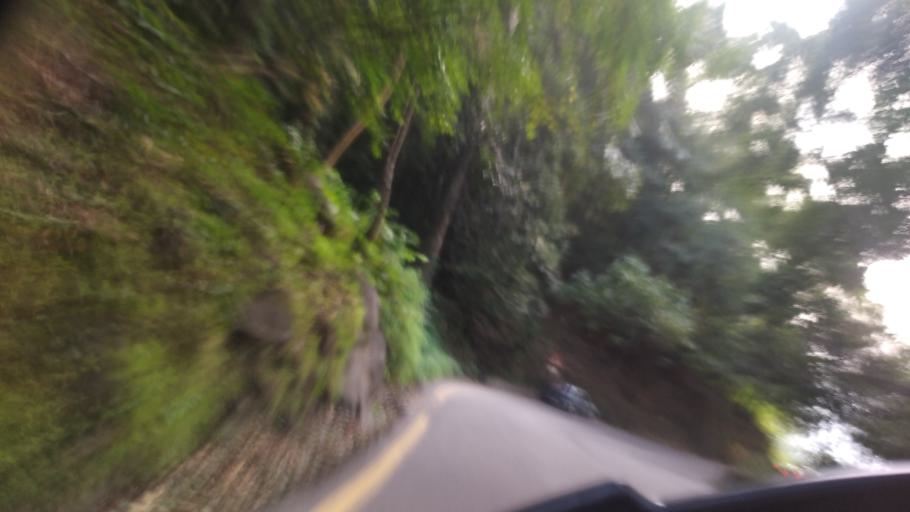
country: IN
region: Kerala
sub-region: Wayanad
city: Kalpetta
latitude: 11.4987
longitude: 76.0244
